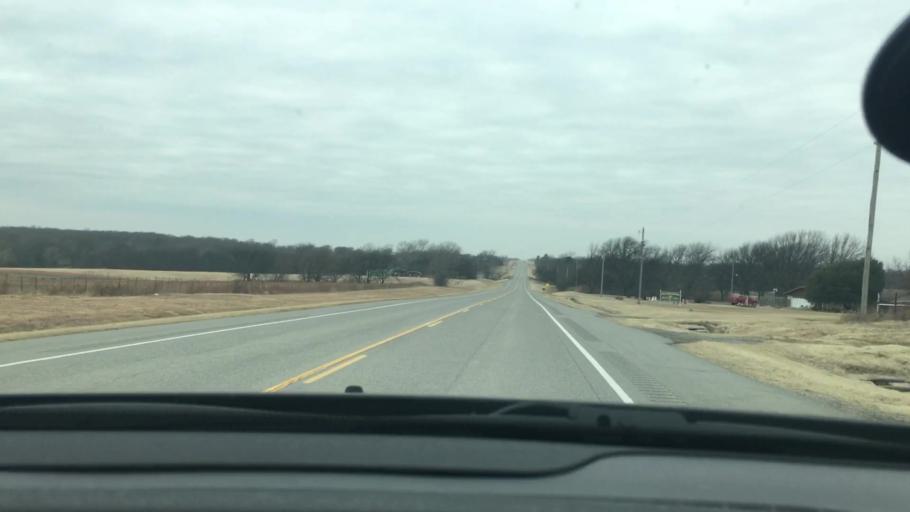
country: US
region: Oklahoma
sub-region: Murray County
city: Davis
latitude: 34.4925
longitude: -97.3738
